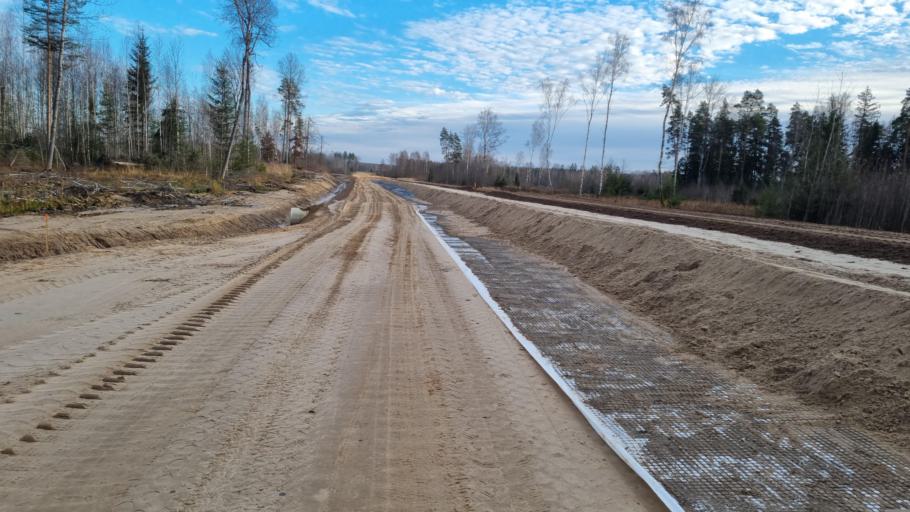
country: LV
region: Kekava
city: Kekava
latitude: 56.7871
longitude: 24.2226
